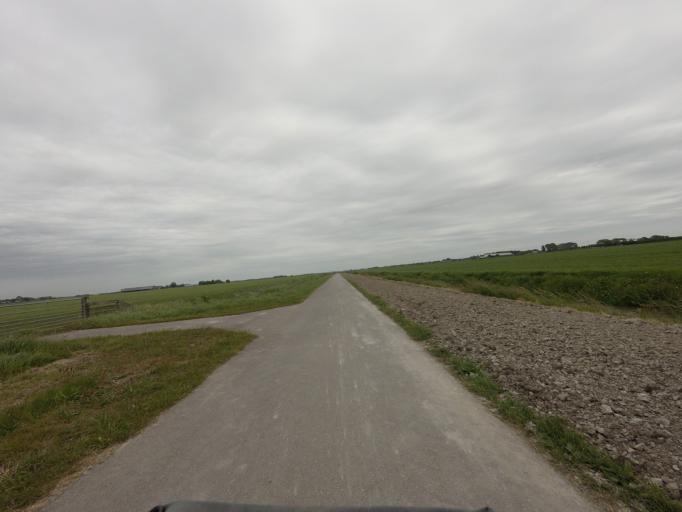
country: NL
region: North Holland
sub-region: Gemeente Medemblik
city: Opperdoes
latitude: 52.7315
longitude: 5.0570
